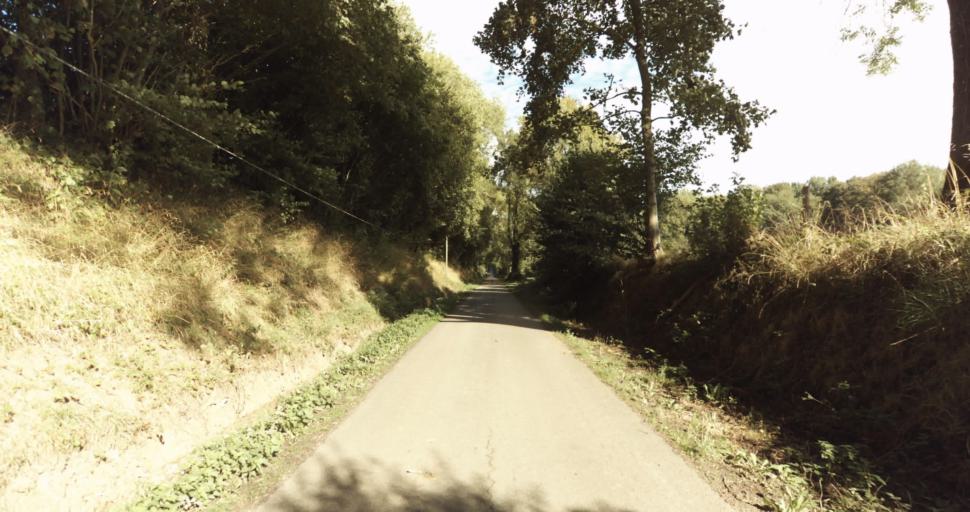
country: FR
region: Lower Normandy
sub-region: Departement de l'Orne
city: Gace
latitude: 48.8079
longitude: 0.2267
